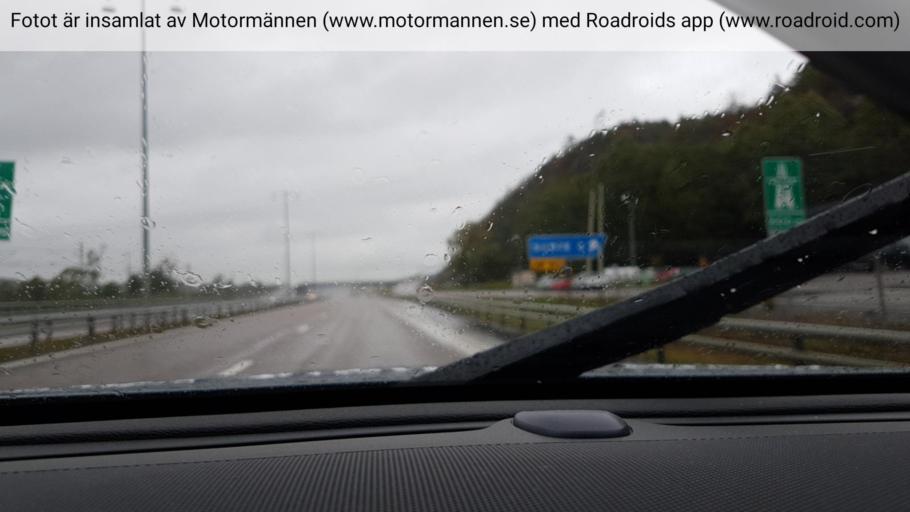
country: SE
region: Vaestra Goetaland
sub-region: Ale Kommun
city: Surte
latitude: 57.8124
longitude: 12.0163
